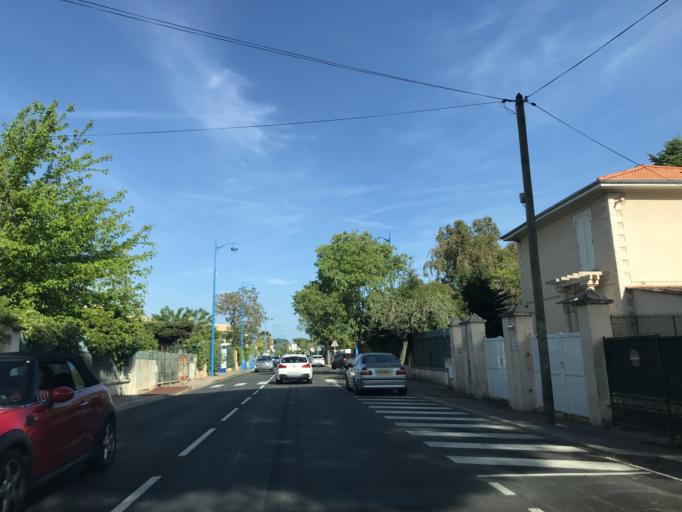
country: FR
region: Provence-Alpes-Cote d'Azur
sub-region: Departement des Alpes-Maritimes
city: Mandelieu-la-Napoule
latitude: 43.5397
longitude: 6.9376
